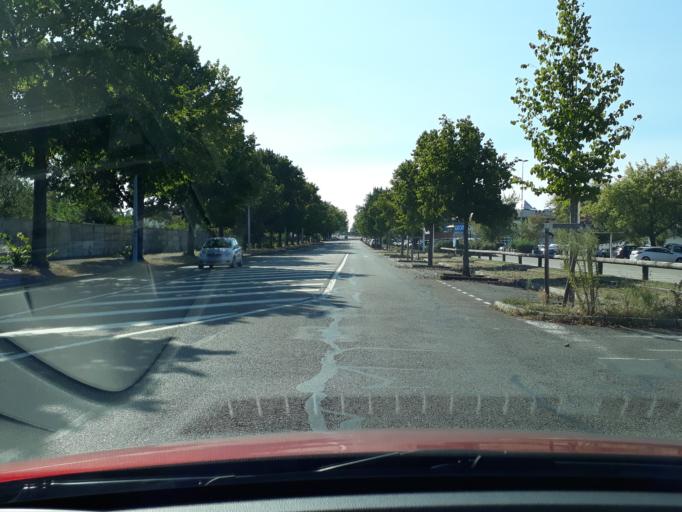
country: FR
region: Rhone-Alpes
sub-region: Departement du Rhone
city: Bron
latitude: 45.7249
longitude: 4.9320
